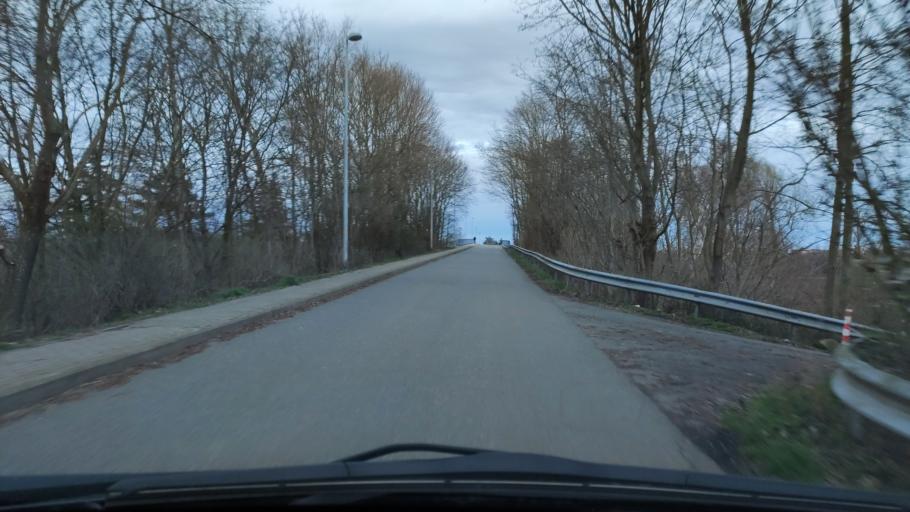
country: DE
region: Baden-Wuerttemberg
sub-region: Karlsruhe Region
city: Hockenheim
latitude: 49.3163
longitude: 8.5339
